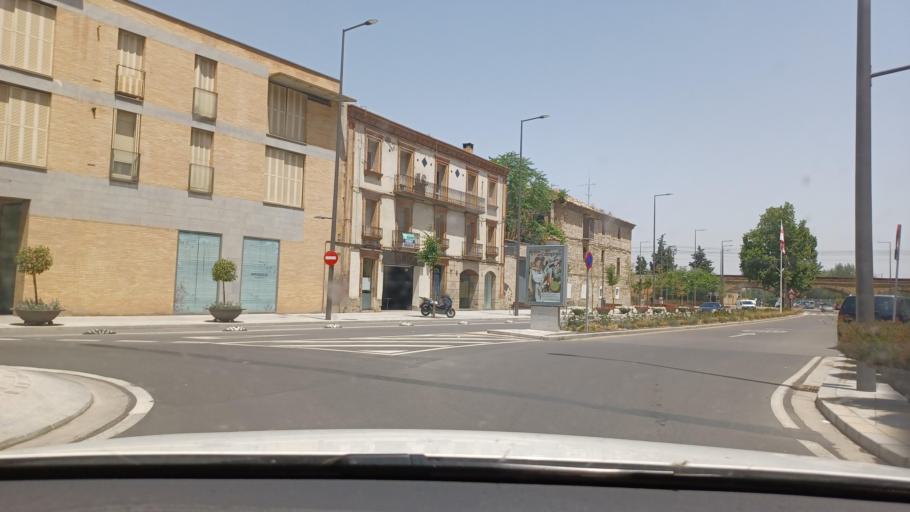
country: ES
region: Navarre
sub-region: Provincia de Navarra
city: Tudela
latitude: 42.0624
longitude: -1.6033
